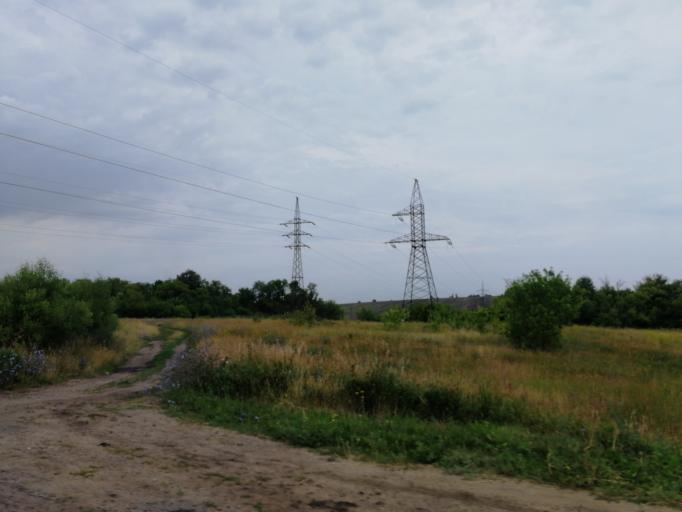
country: RU
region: Tula
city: Bogoroditsk
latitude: 53.7172
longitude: 38.1239
